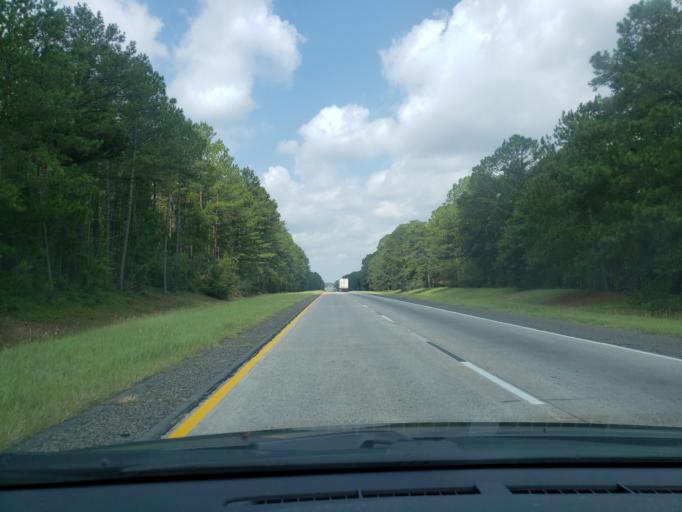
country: US
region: Georgia
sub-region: Treutlen County
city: Soperton
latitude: 32.4273
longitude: -82.5543
